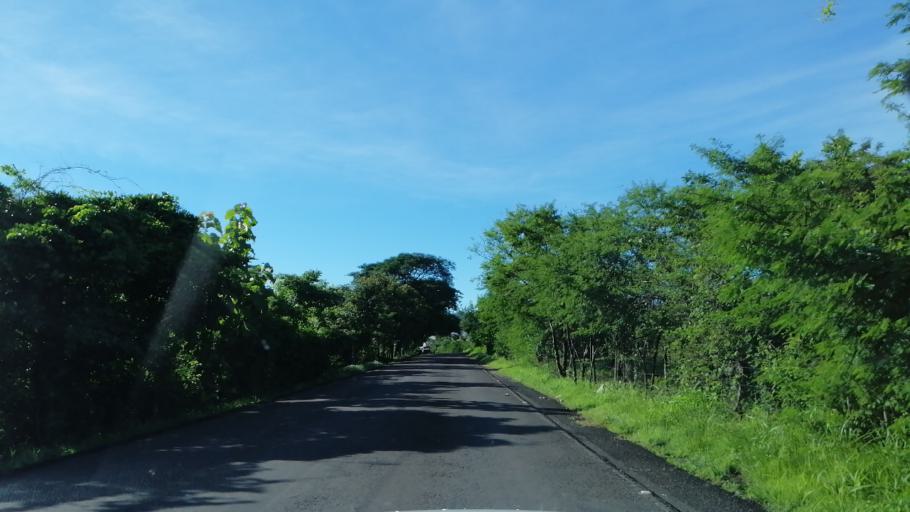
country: SV
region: Morazan
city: Cacaopera
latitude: 13.7836
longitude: -88.1053
